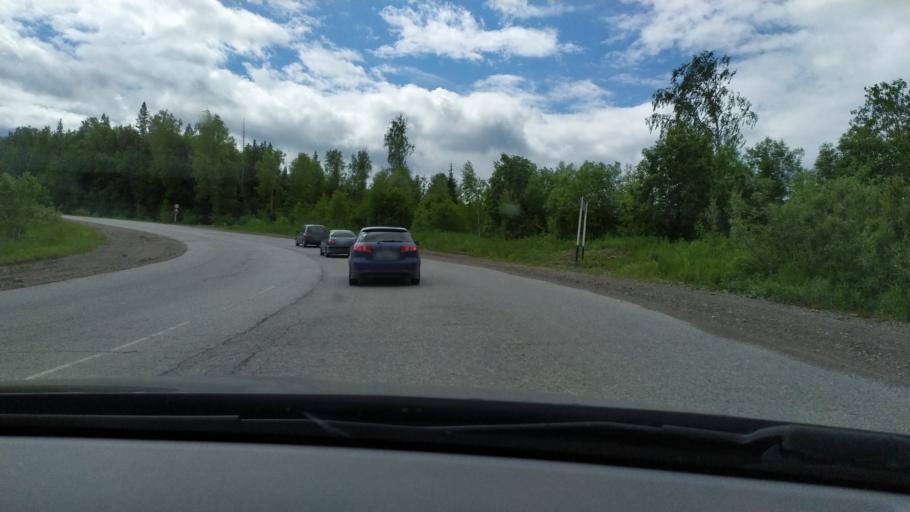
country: RU
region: Perm
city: Gremyachinsk
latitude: 58.4394
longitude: 57.8847
